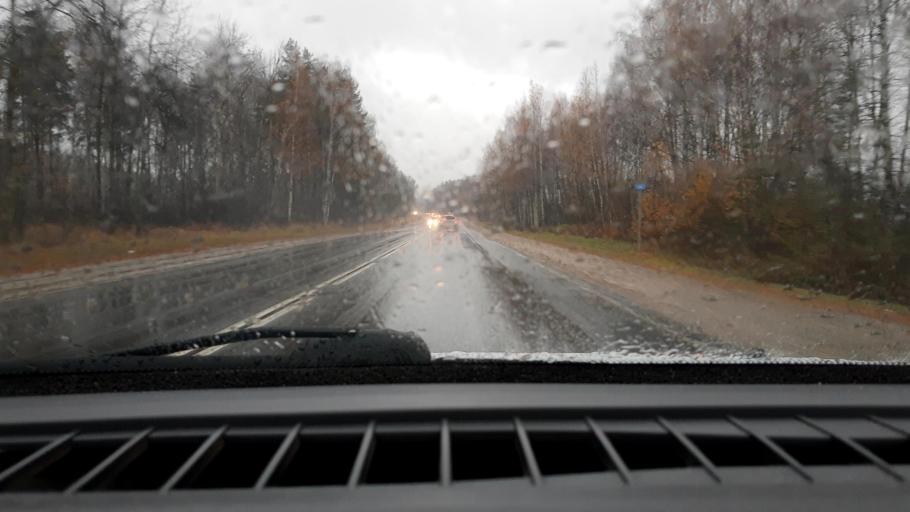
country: RU
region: Nizjnij Novgorod
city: Sitniki
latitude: 56.4560
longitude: 44.0223
